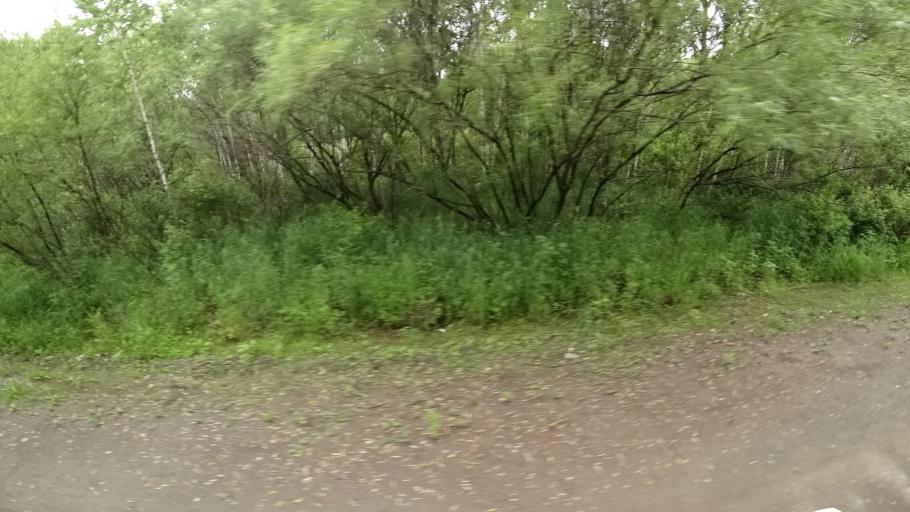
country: RU
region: Khabarovsk Krai
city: Amursk
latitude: 49.9131
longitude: 136.1586
